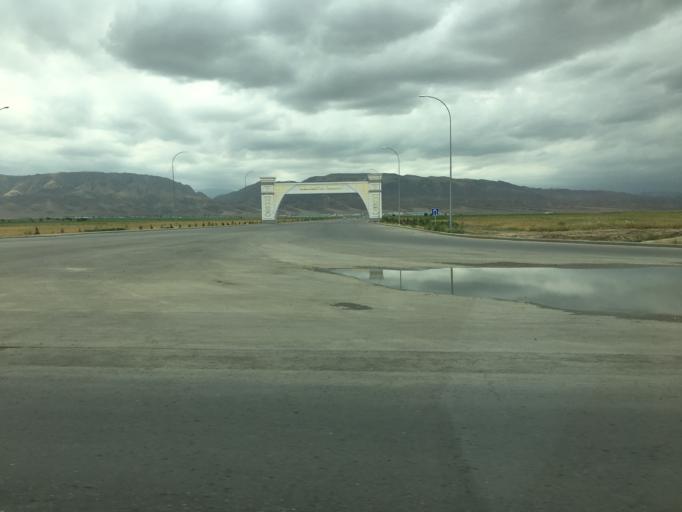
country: TM
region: Ahal
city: Annau
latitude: 37.8359
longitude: 58.7327
